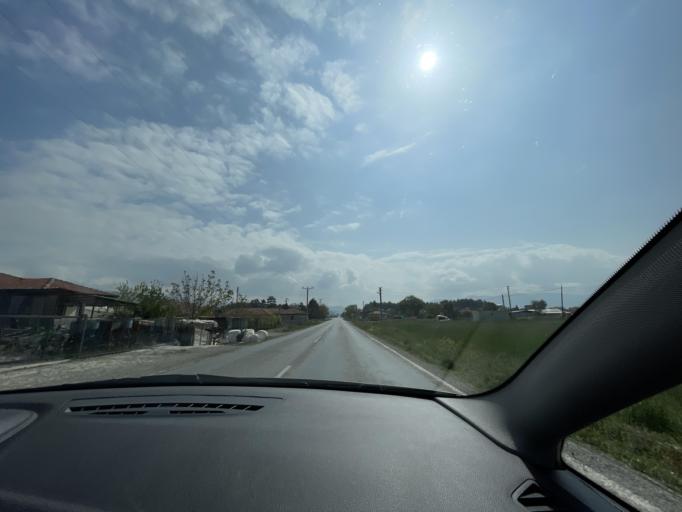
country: TR
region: Denizli
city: Acipayam
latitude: 37.5079
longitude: 29.3995
